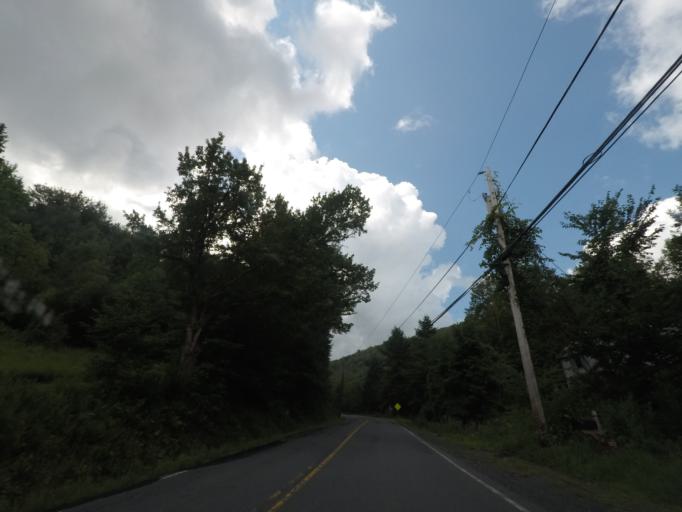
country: US
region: New York
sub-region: Rensselaer County
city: Averill Park
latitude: 42.6863
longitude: -73.3823
